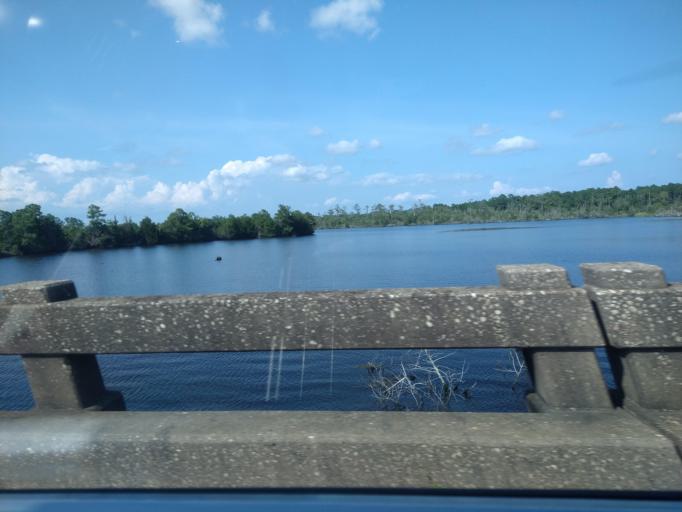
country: US
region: North Carolina
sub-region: Onslow County
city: Piney Green
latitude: 34.7349
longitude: -77.3538
